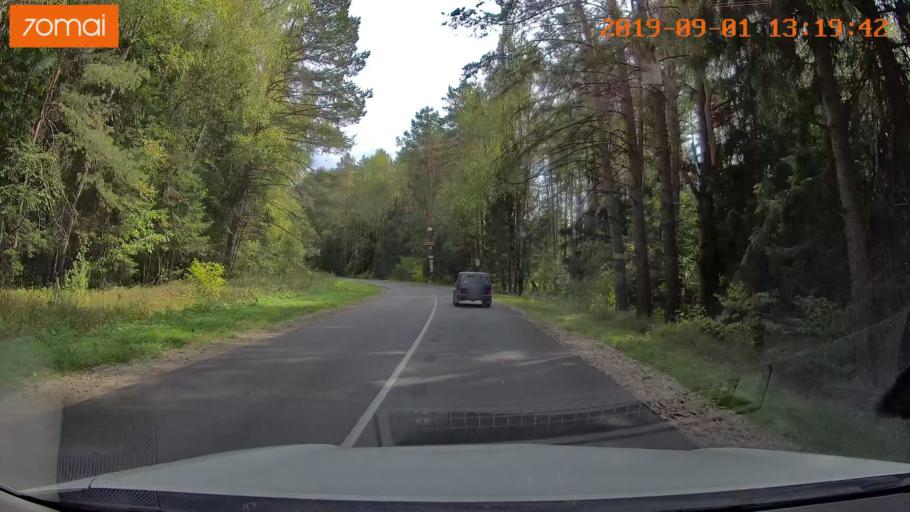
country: RU
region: Kaluga
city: Maloyaroslavets
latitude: 54.9153
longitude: 36.4838
